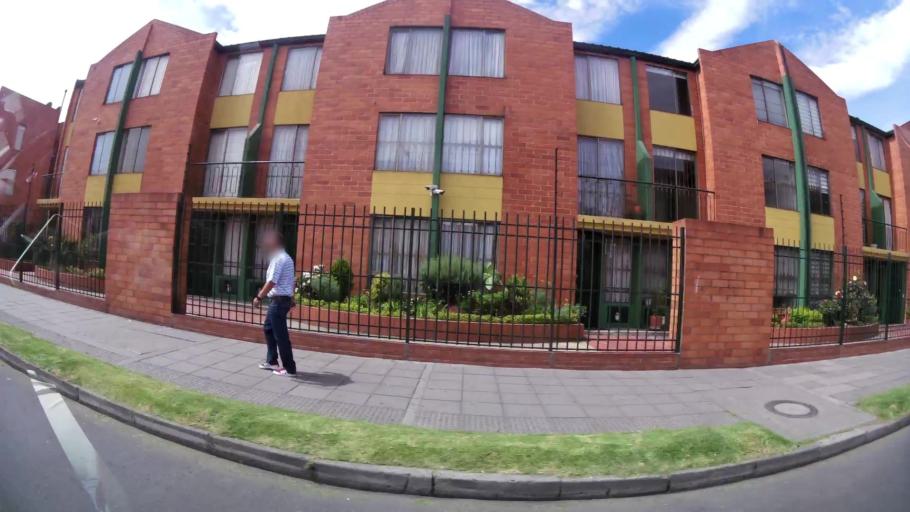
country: CO
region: Bogota D.C.
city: Bogota
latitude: 4.6179
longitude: -74.1323
